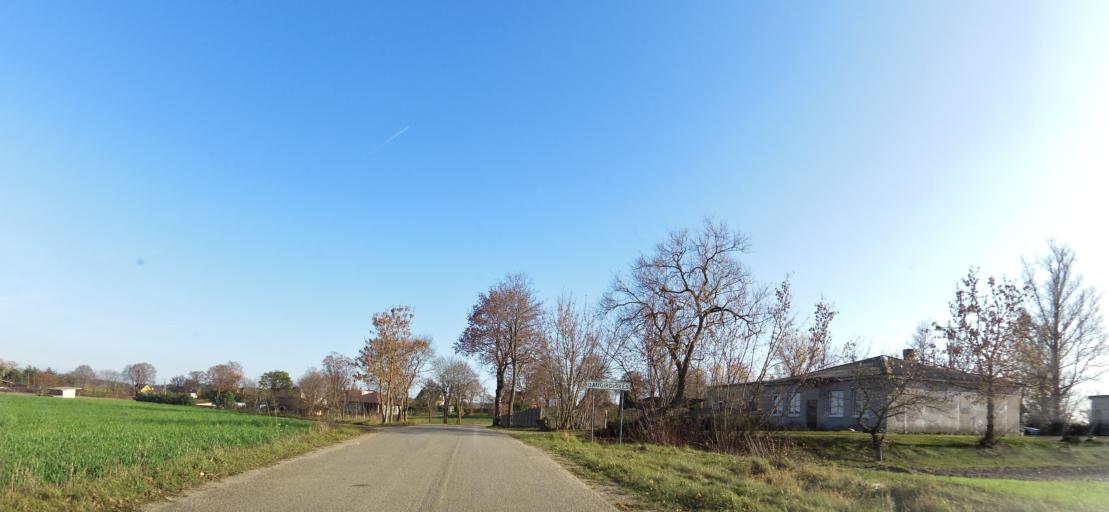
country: LT
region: Vilnius County
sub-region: Vilniaus Rajonas
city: Vievis
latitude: 54.6473
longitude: 24.7407
